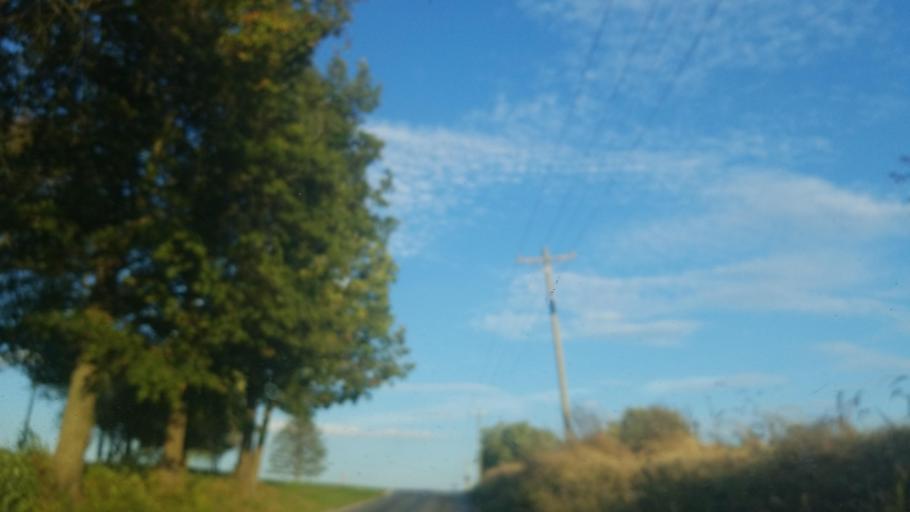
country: US
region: Illinois
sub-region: Saline County
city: Carrier Mills
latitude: 37.8050
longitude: -88.6429
